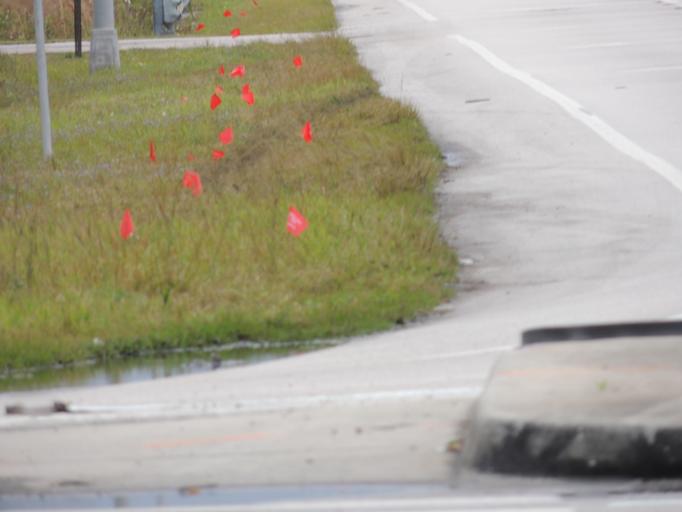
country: US
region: Florida
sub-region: Osceola County
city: Buenaventura Lakes
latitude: 28.2846
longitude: -81.3516
